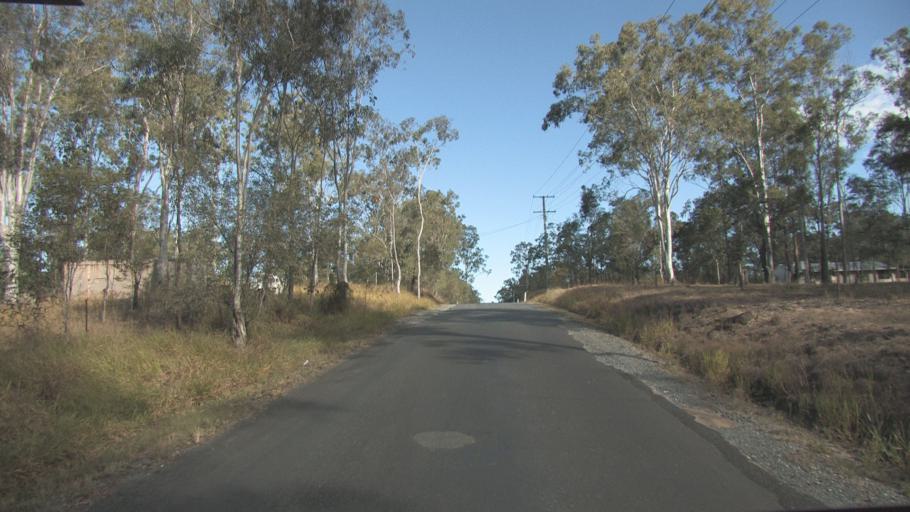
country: AU
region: Queensland
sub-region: Logan
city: Cedar Vale
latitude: -27.8264
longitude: 153.0624
